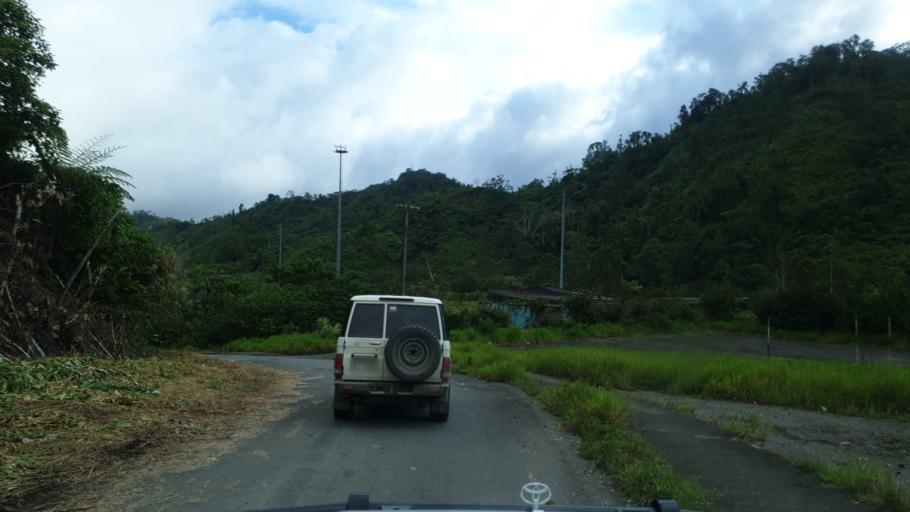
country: PG
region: Bougainville
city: Panguna
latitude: -6.3054
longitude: 155.4879
